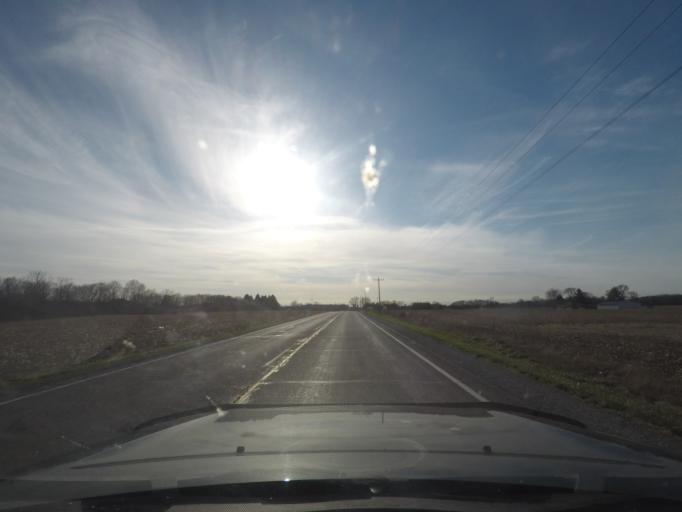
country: US
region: Indiana
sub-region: Marshall County
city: Plymouth
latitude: 41.4490
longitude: -86.3454
